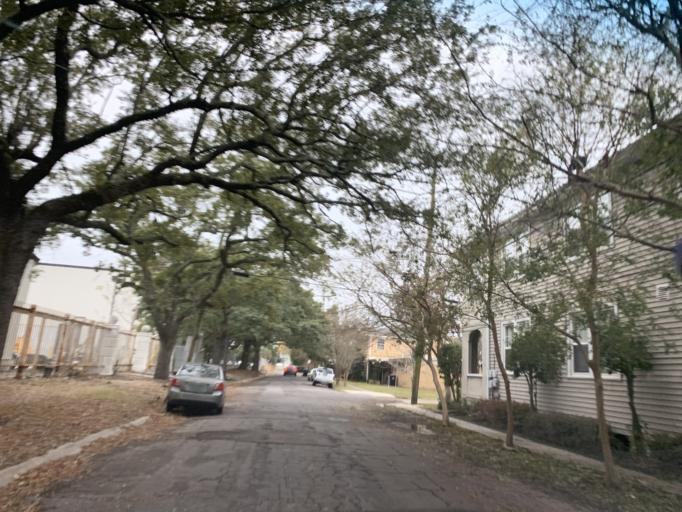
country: US
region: Louisiana
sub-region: Orleans Parish
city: New Orleans
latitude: 29.9865
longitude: -90.1073
